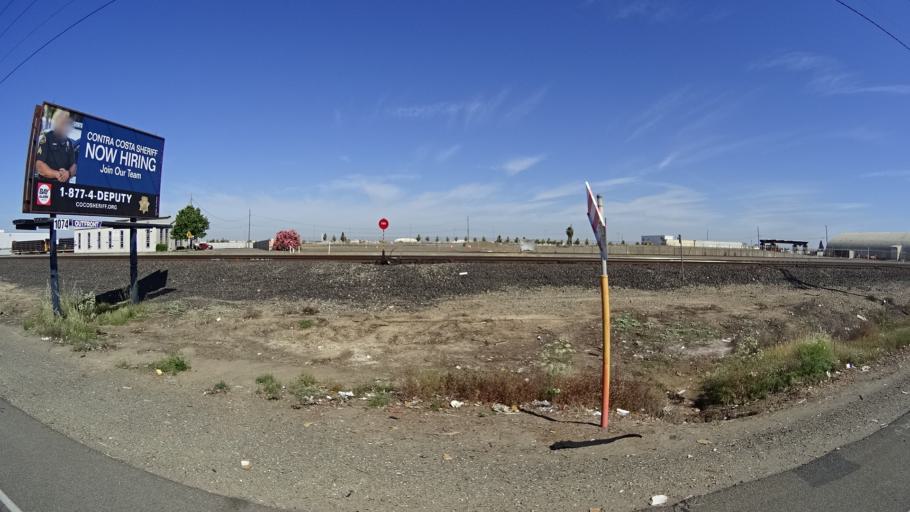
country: US
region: California
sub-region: Sacramento County
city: North Highlands
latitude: 38.6472
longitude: -121.3957
